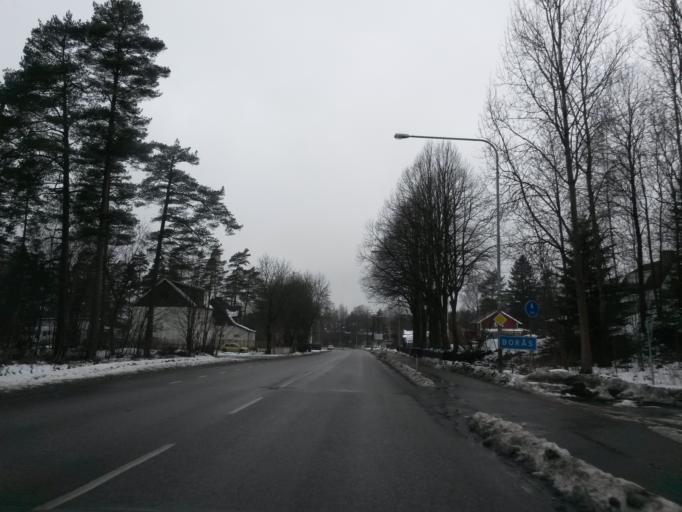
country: SE
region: Vaestra Goetaland
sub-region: Boras Kommun
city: Ganghester
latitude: 57.7026
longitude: 12.9815
